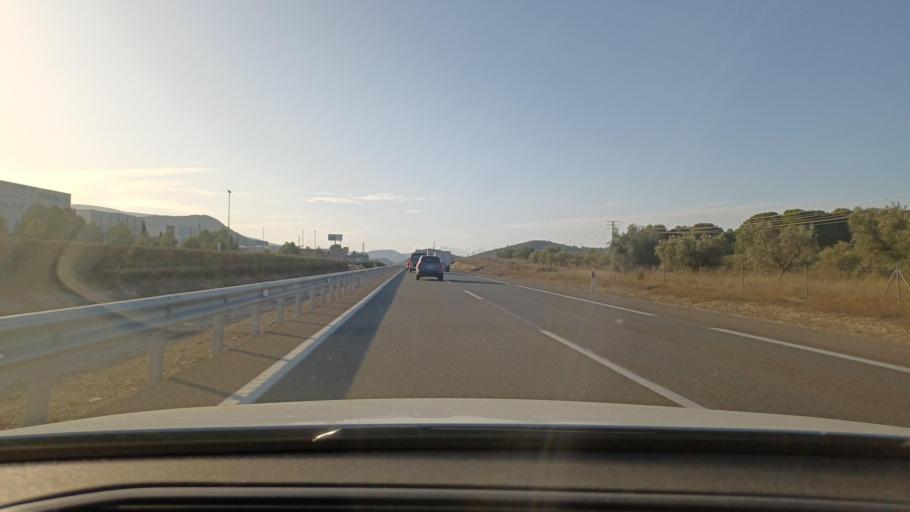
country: ES
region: Valencia
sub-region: Provincia de Alicante
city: Elda
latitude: 38.5074
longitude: -0.7945
